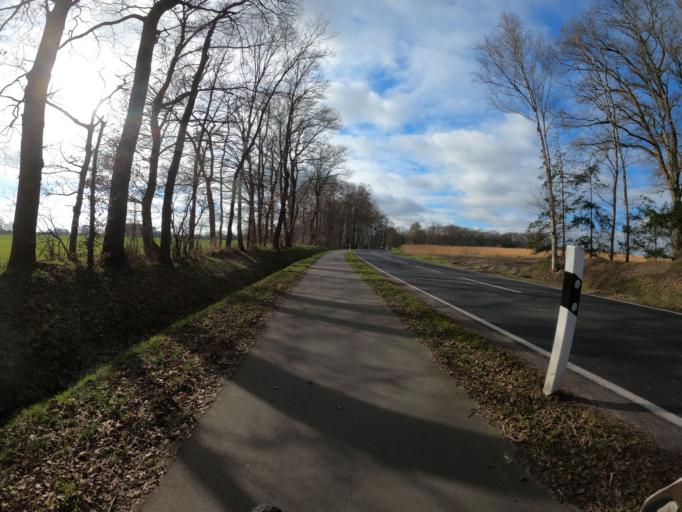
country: DE
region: Lower Saxony
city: Dohren
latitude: 52.6666
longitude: 7.5393
